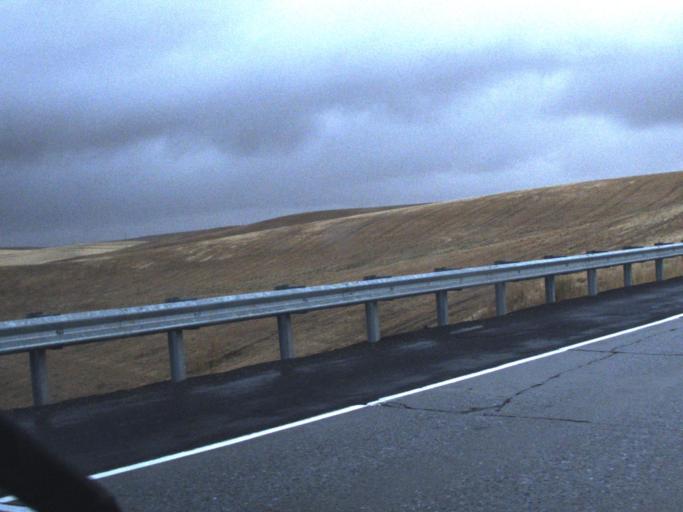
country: US
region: Washington
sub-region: Whitman County
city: Colfax
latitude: 47.1689
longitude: -117.3799
